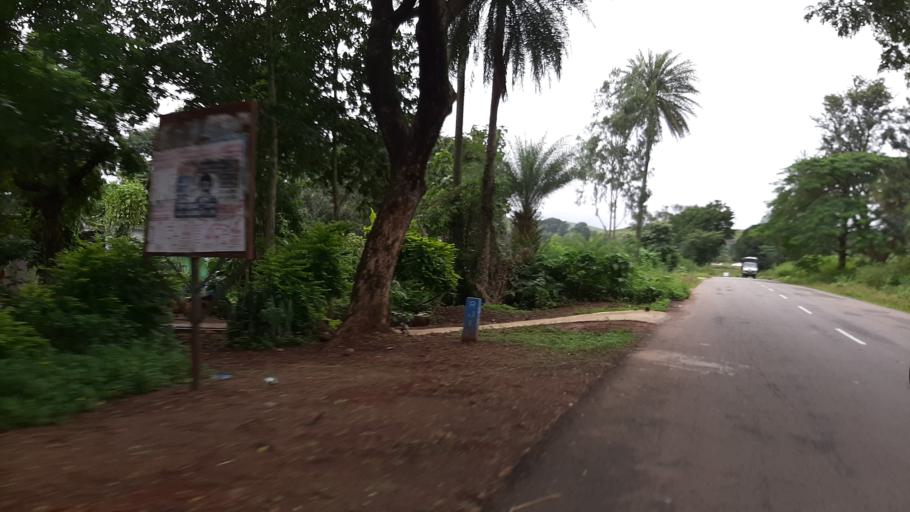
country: IN
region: Andhra Pradesh
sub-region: Vizianagaram District
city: Salur
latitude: 18.3014
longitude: 82.9107
